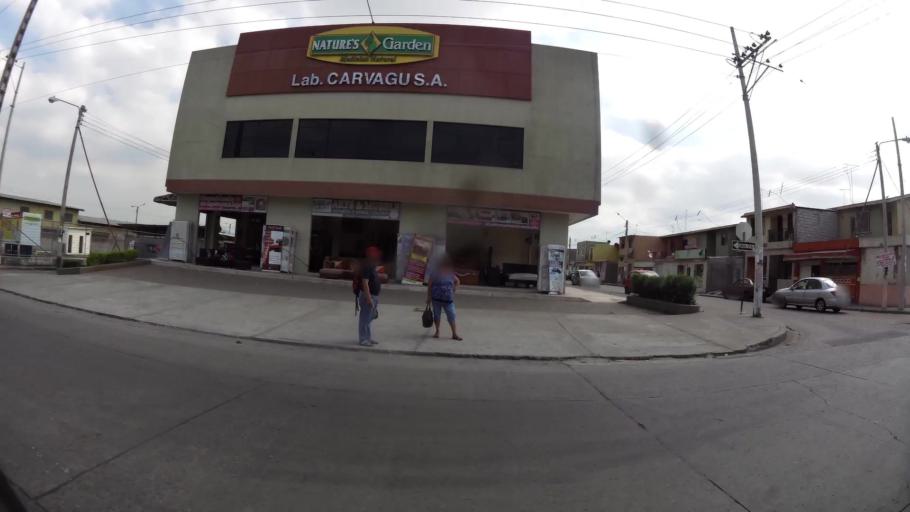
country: EC
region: Guayas
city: Eloy Alfaro
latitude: -2.0800
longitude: -79.9160
